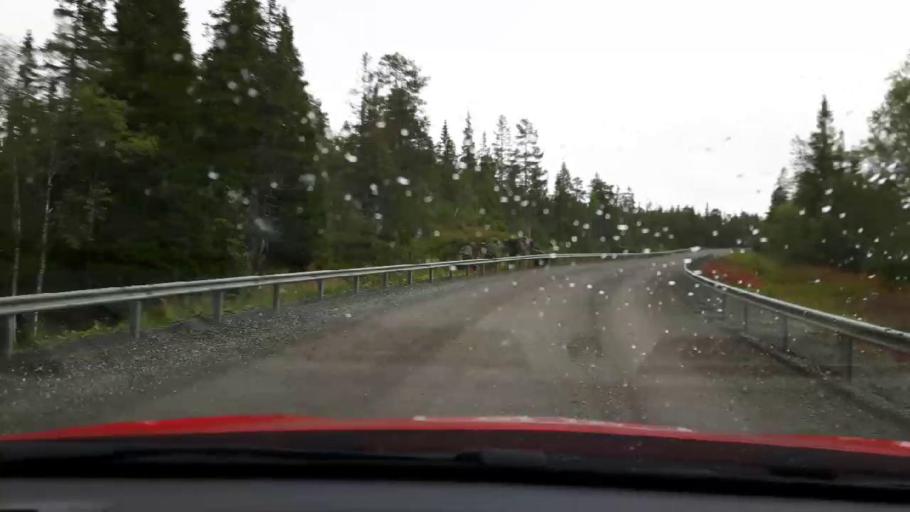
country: NO
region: Nord-Trondelag
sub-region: Meraker
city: Meraker
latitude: 63.6432
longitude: 12.2709
